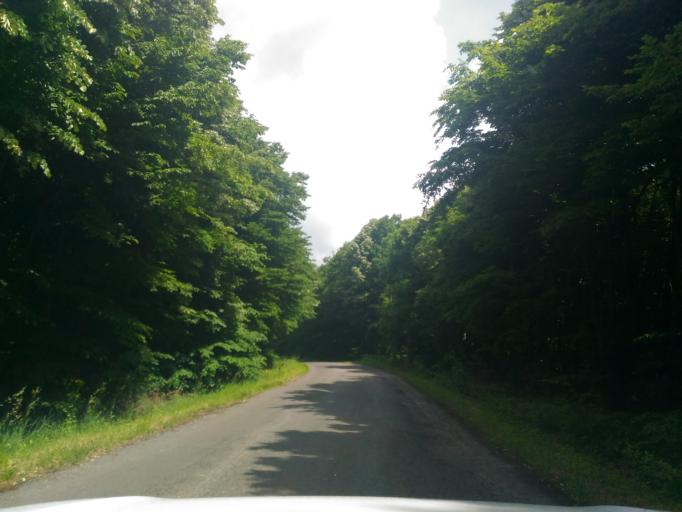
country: HU
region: Baranya
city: Pecs
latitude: 46.1313
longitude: 18.2316
